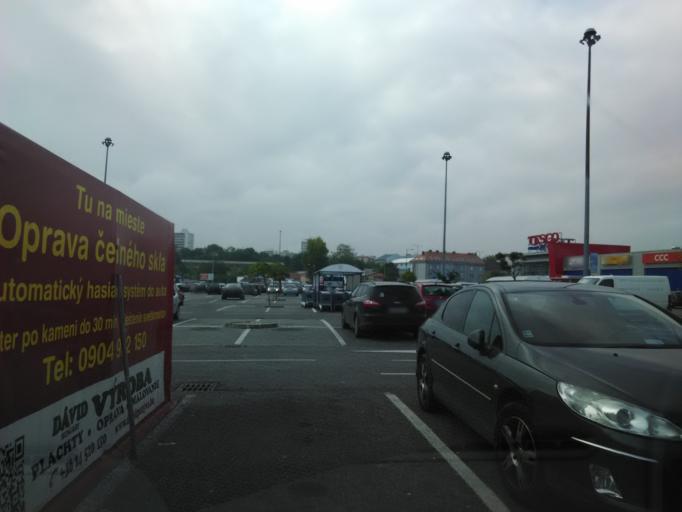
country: SK
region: Nitriansky
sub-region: Okres Nitra
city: Nitra
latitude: 48.3115
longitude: 18.0715
